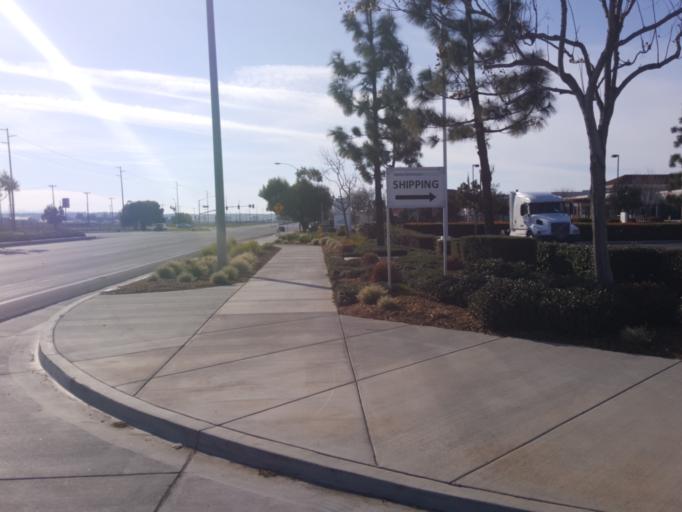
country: US
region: California
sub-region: Riverside County
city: March Air Force Base
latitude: 33.9104
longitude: -117.2497
